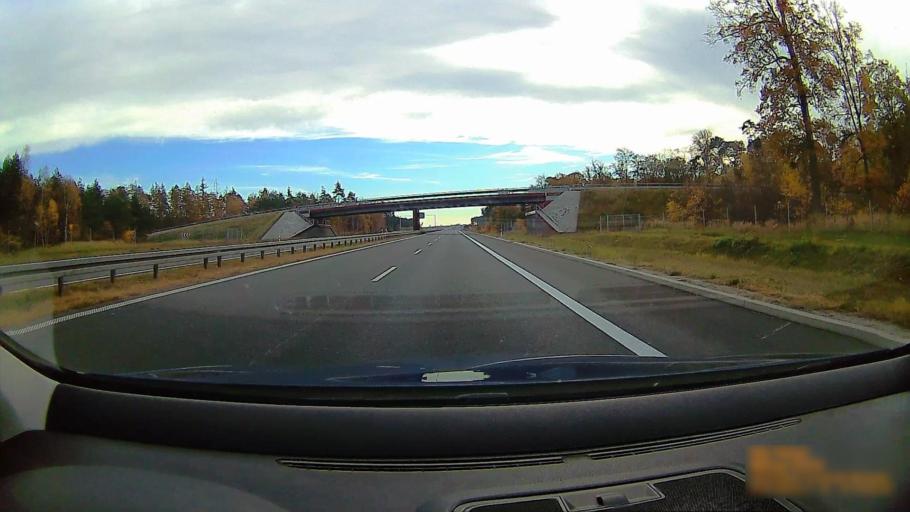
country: PL
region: Greater Poland Voivodeship
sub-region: Powiat ostrowski
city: Ostrow Wielkopolski
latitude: 51.6561
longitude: 17.8649
